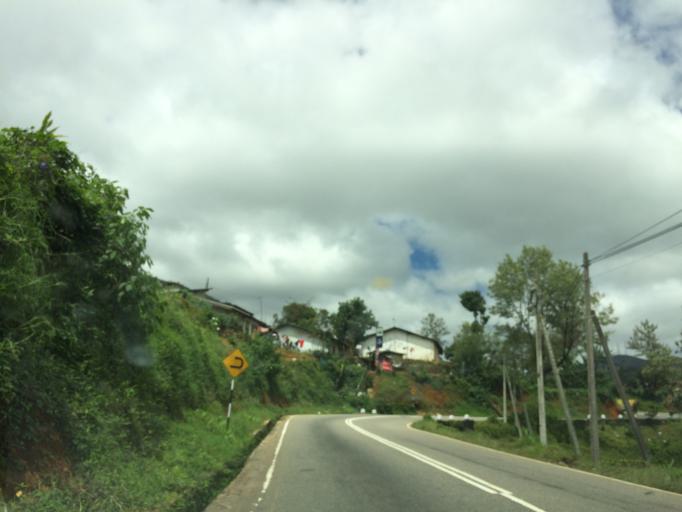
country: LK
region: Central
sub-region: Nuwara Eliya District
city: Nuwara Eliya
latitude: 7.0217
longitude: 80.7225
